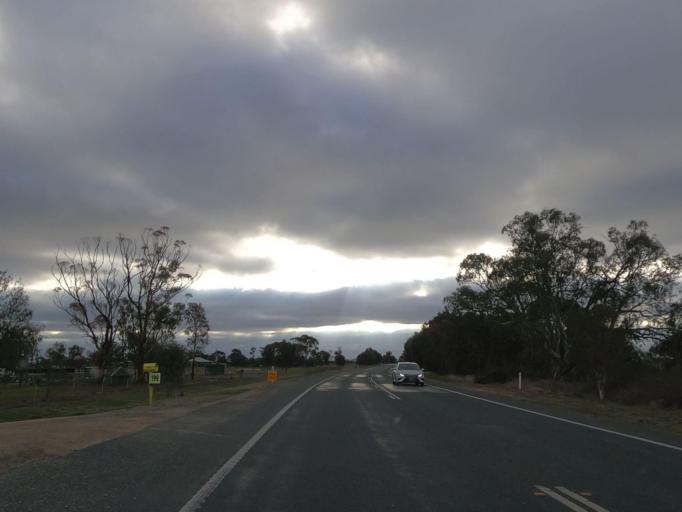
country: AU
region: Victoria
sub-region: Swan Hill
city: Swan Hill
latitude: -35.7322
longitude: 143.8965
